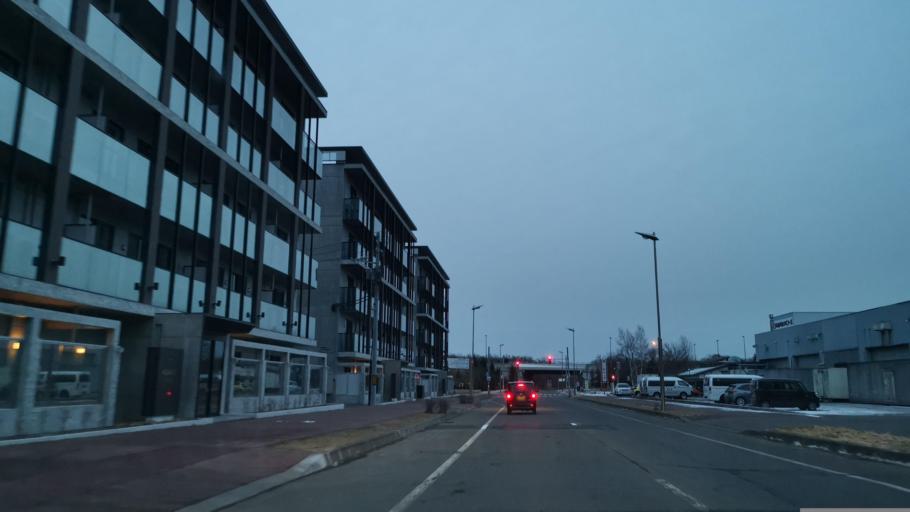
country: JP
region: Hokkaido
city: Chitose
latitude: 42.8148
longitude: 141.6767
